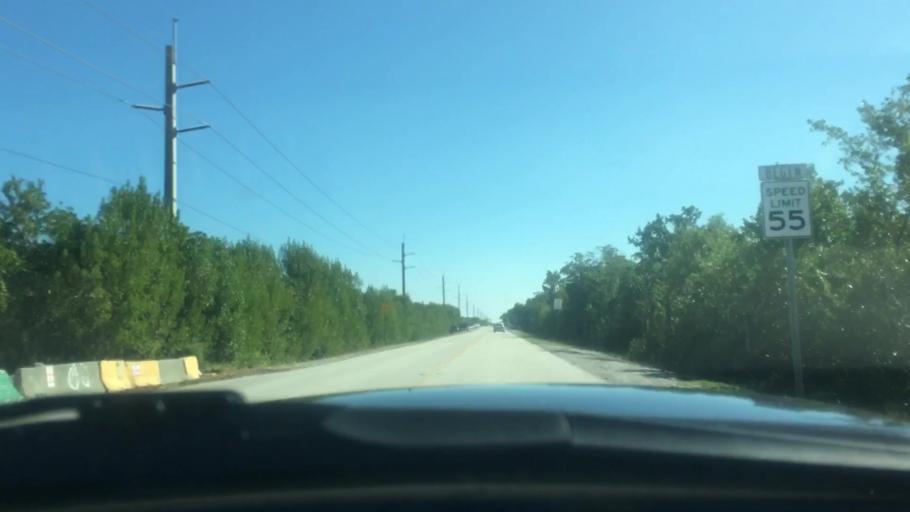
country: US
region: Florida
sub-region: Monroe County
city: North Key Largo
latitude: 25.2847
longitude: -80.3613
